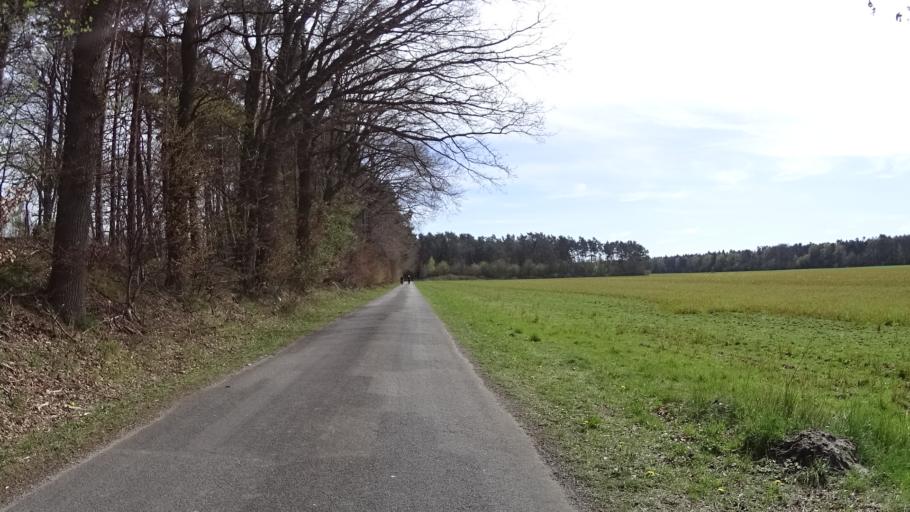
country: DE
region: Lower Saxony
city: Lunne
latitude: 52.3889
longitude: 7.3905
